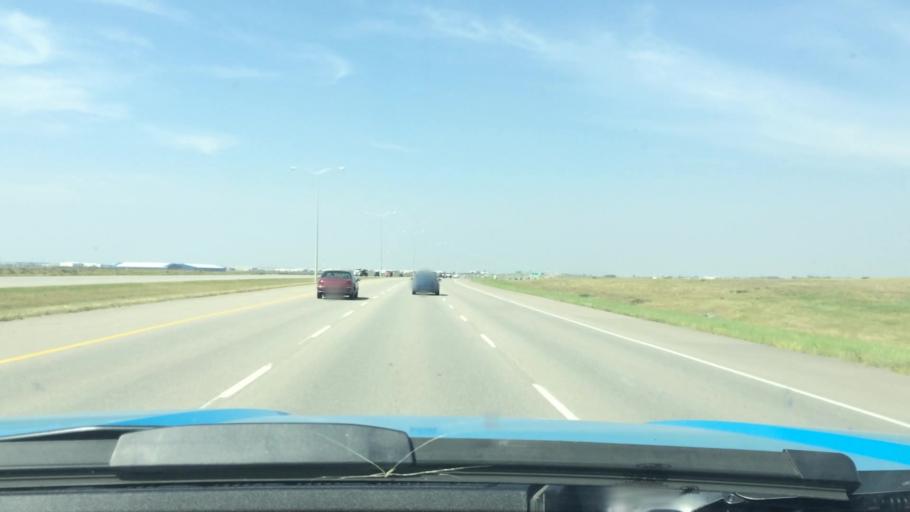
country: CA
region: Alberta
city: Chestermere
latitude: 50.9275
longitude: -113.9188
